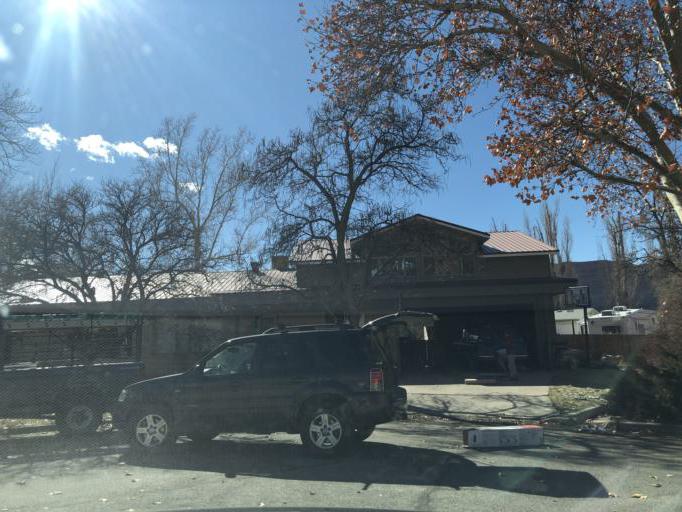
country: US
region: Utah
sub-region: Grand County
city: Moab
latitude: 38.5851
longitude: -109.5602
